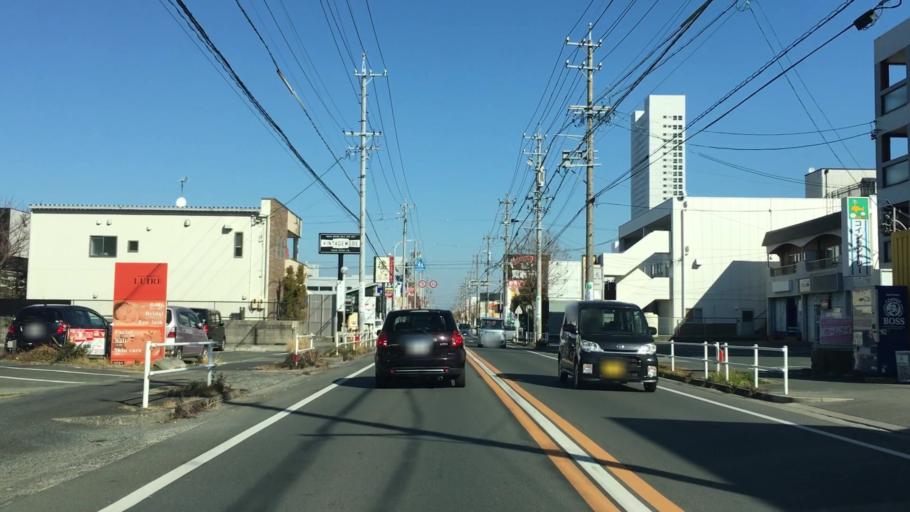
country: JP
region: Aichi
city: Toyohashi
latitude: 34.7414
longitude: 137.3673
